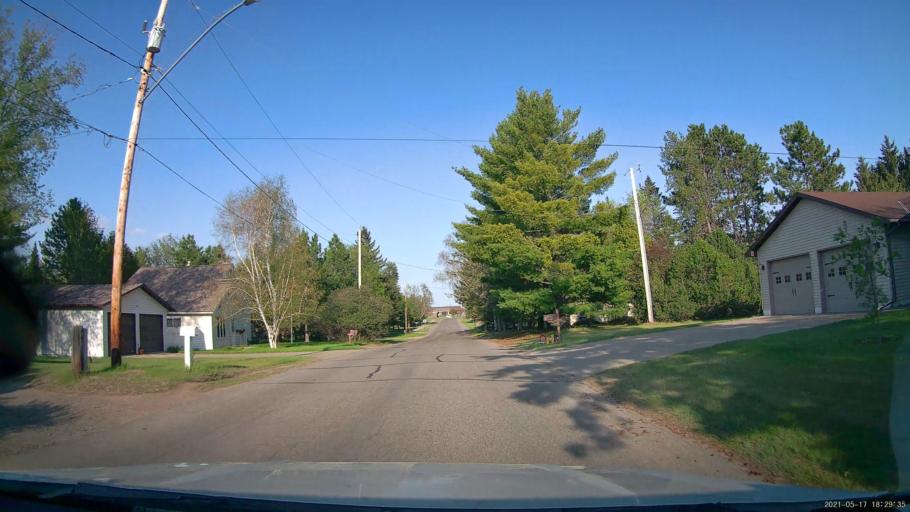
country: US
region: Minnesota
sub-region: Hubbard County
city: Park Rapids
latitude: 46.9253
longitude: -95.0459
